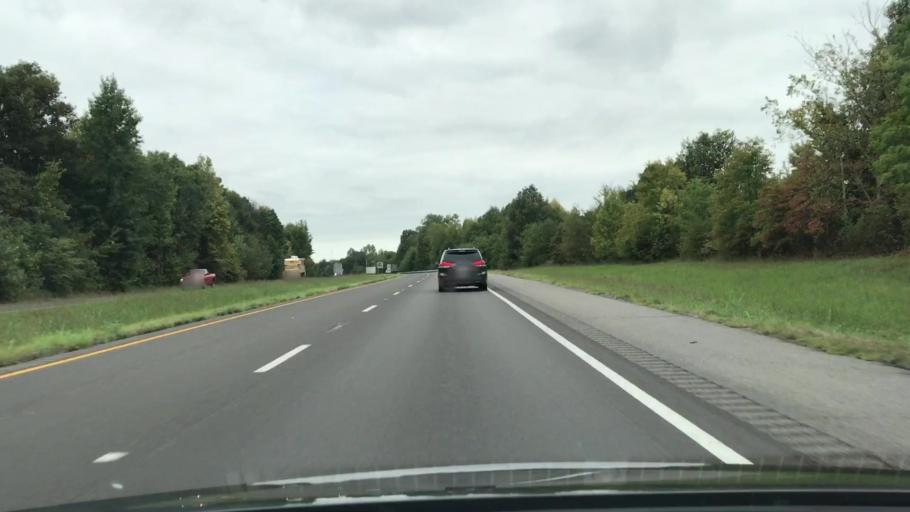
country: US
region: Kentucky
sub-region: Fulton County
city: Fulton
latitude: 36.5882
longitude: -88.8176
